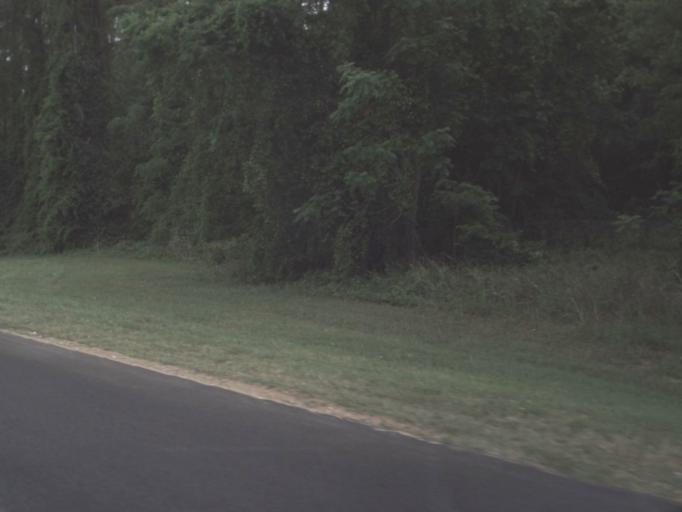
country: US
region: Florida
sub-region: Marion County
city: Citra
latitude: 29.3705
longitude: -82.2283
